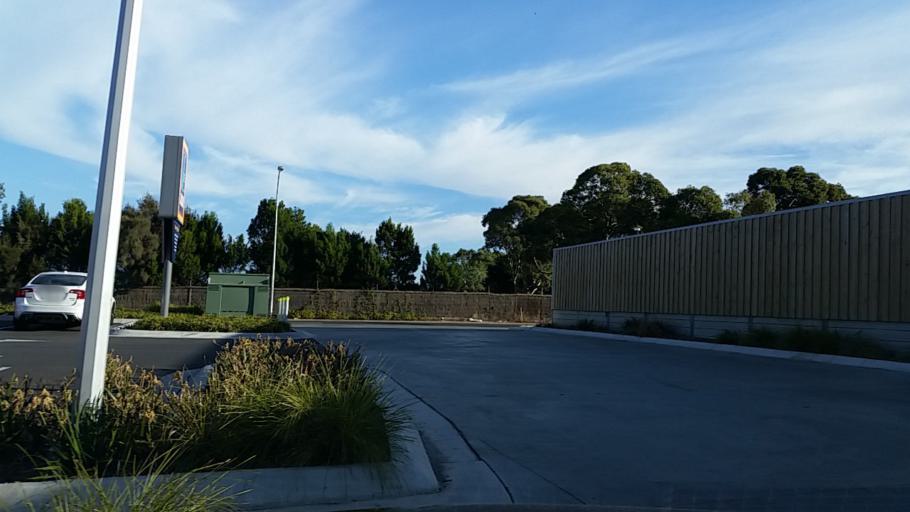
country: AU
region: South Australia
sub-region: Charles Sturt
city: Royal Park
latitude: -34.8811
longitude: 138.5028
